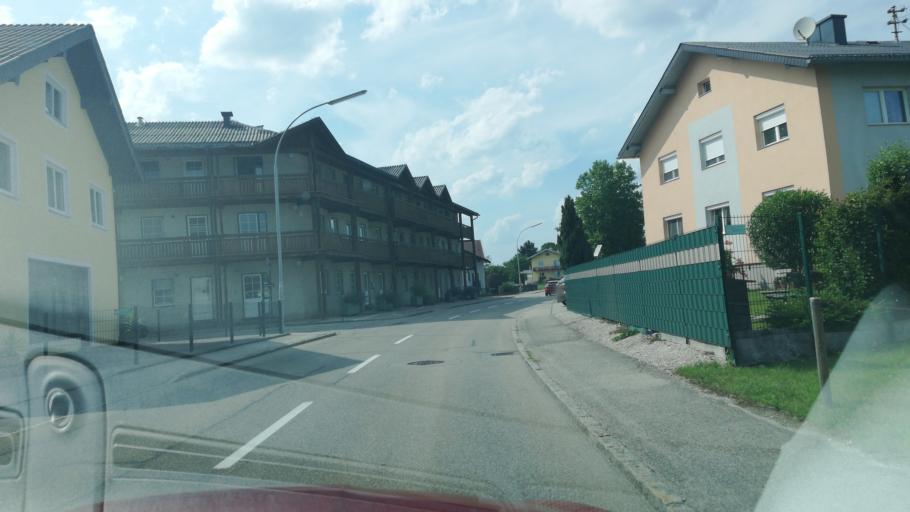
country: AT
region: Upper Austria
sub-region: Politischer Bezirk Vocklabruck
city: Attnang-Puchheim
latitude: 48.0178
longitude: 13.7165
